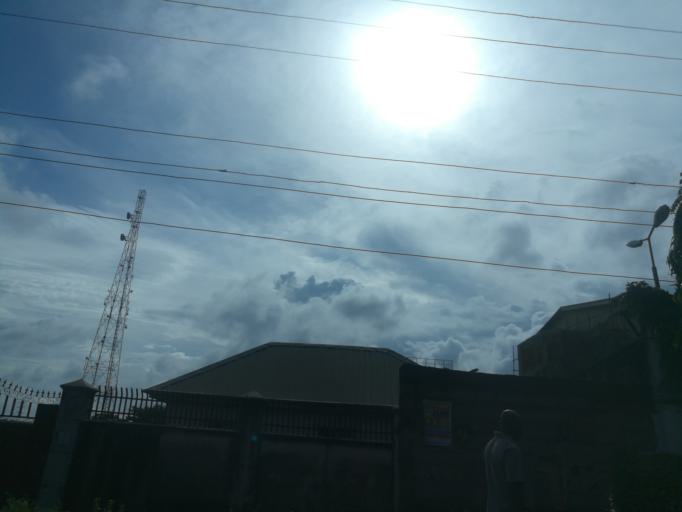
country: NG
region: Lagos
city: Agege
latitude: 6.6248
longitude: 3.3499
